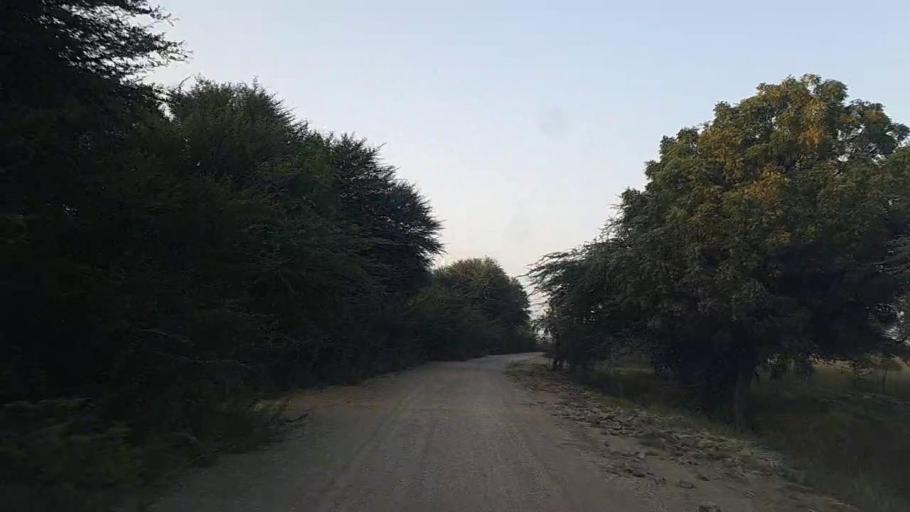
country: PK
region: Sindh
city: Naukot
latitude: 24.7007
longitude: 69.2732
